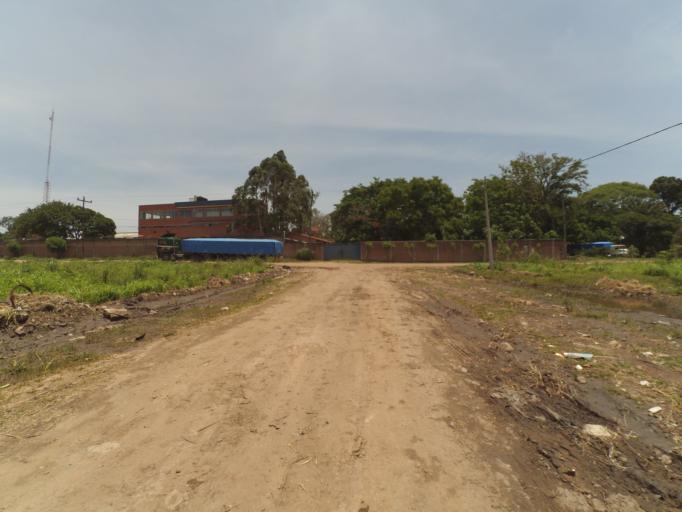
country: BO
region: Santa Cruz
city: Santa Cruz de la Sierra
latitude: -17.8397
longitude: -63.2425
